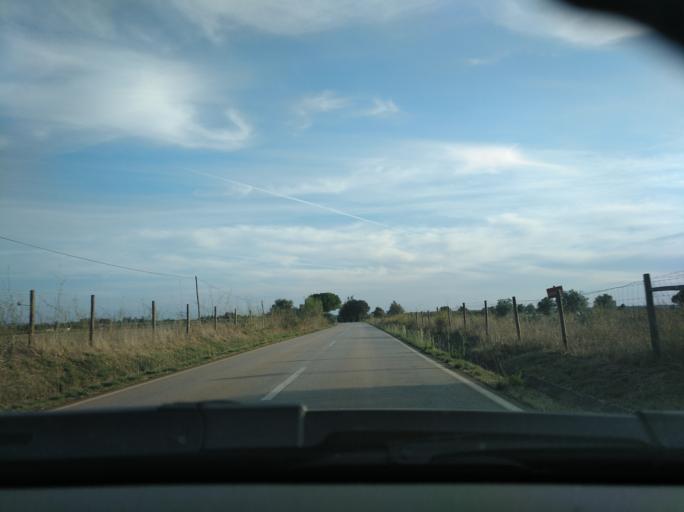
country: PT
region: Portalegre
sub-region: Avis
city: Avis
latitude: 38.9357
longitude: -7.8091
